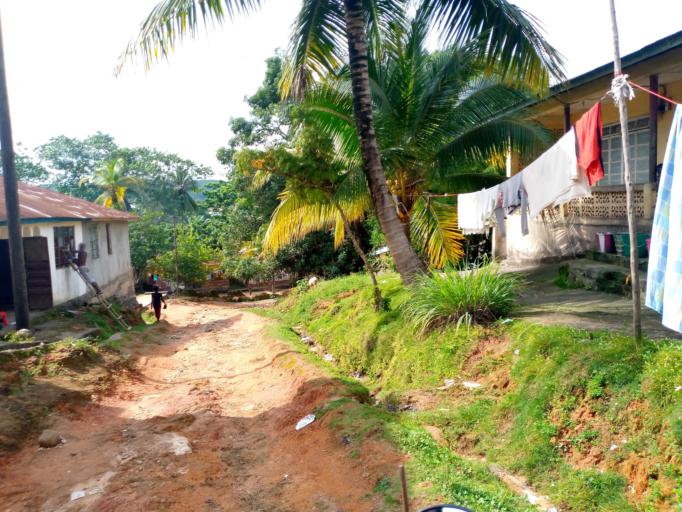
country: SL
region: Northern Province
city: Magburaka
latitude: 8.7281
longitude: -11.9472
